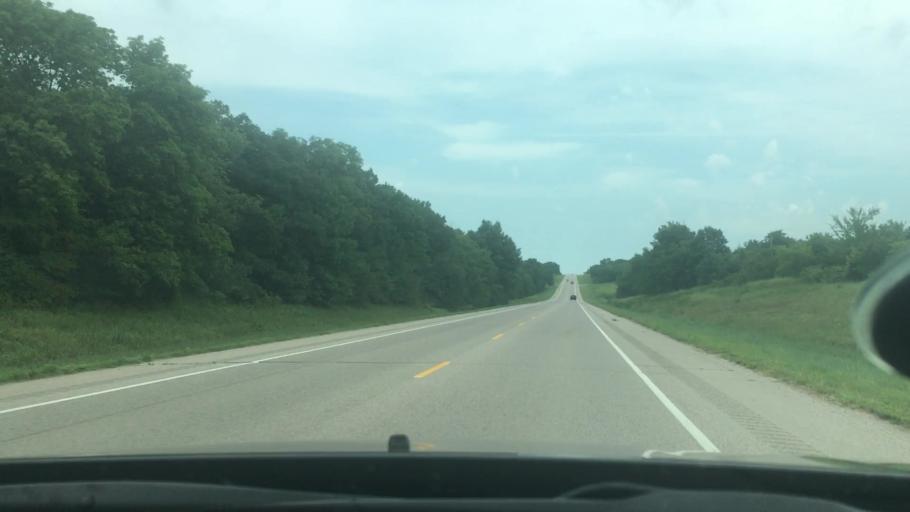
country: US
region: Oklahoma
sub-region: Seminole County
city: Konawa
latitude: 35.0047
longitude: -96.6788
